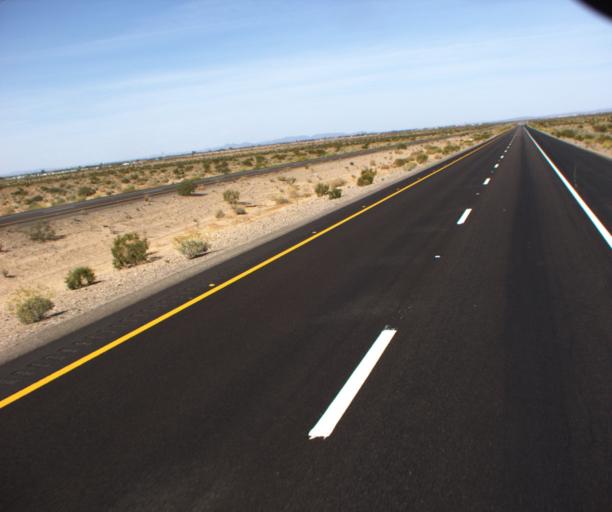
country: US
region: Arizona
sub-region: Yuma County
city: Somerton
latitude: 32.5669
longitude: -114.5583
